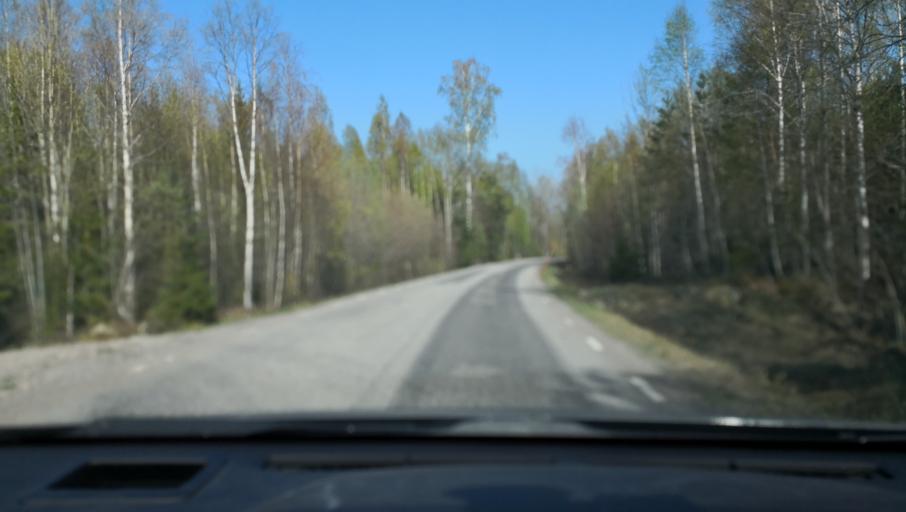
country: SE
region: Uppsala
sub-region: Heby Kommun
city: Heby
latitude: 60.0432
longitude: 16.8389
